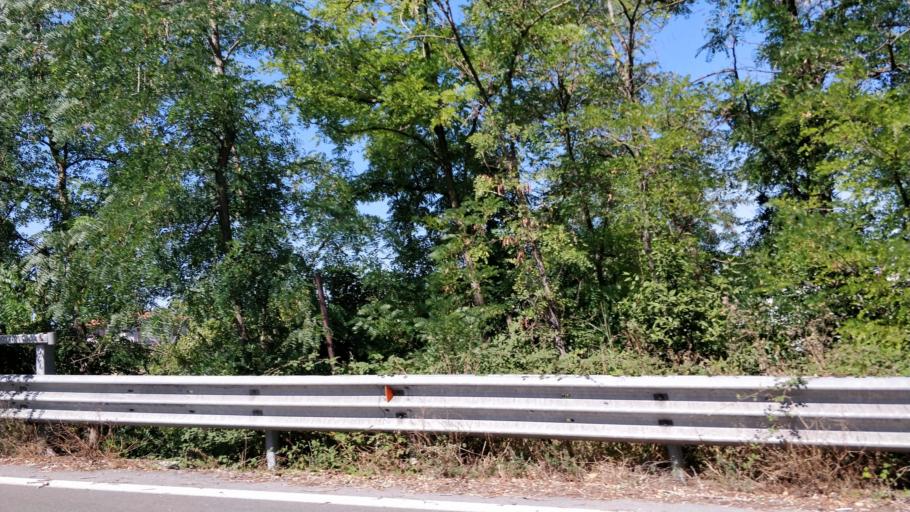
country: IT
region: Abruzzo
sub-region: Provincia di Chieti
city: Chieti
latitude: 42.3933
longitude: 14.1627
